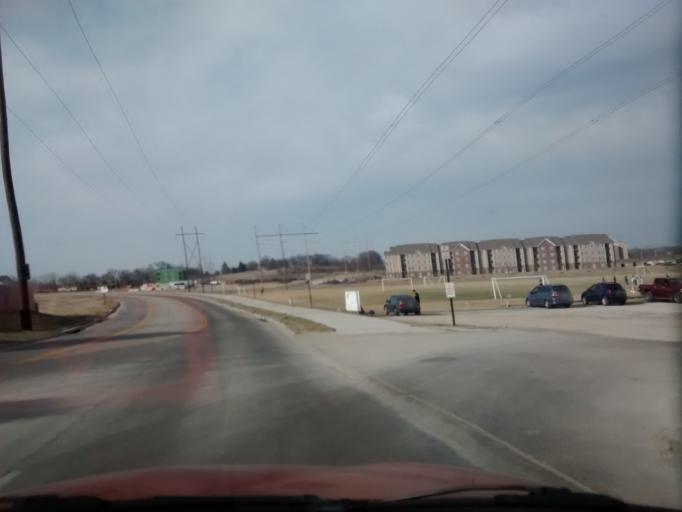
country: US
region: Nebraska
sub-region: Sarpy County
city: Offutt Air Force Base
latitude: 41.1426
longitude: -95.9761
